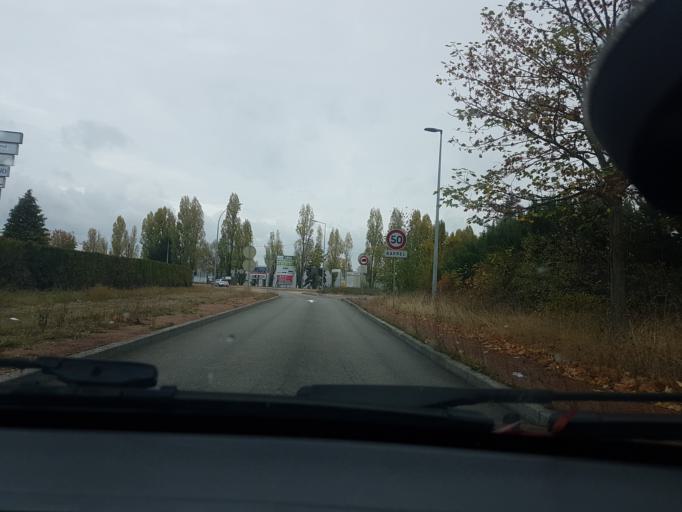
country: FR
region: Bourgogne
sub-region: Departement de la Cote-d'Or
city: Saint-Apollinaire
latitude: 47.3377
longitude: 5.0722
